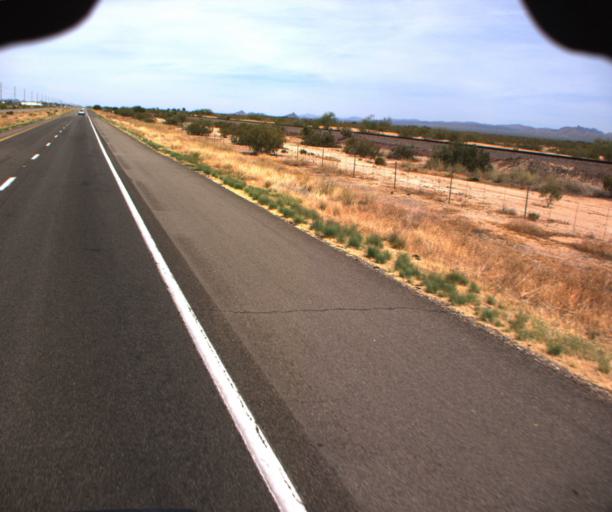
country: US
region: Arizona
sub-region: Maricopa County
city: Sun City West
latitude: 33.7573
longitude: -112.5020
